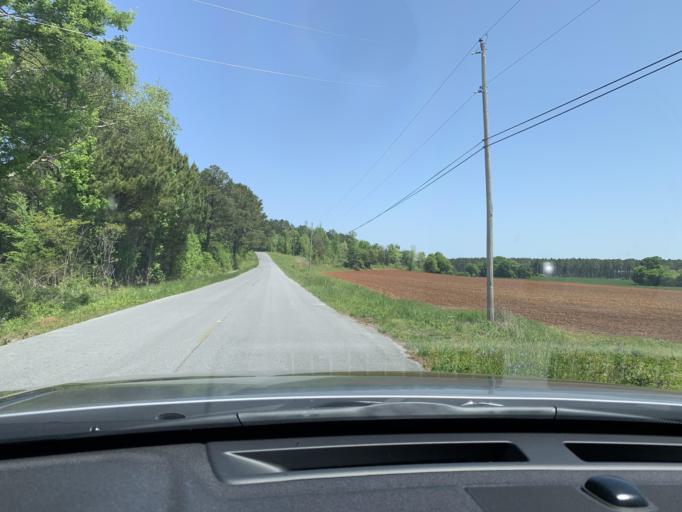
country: US
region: Georgia
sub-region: Polk County
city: Cedartown
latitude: 34.0418
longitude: -85.1896
